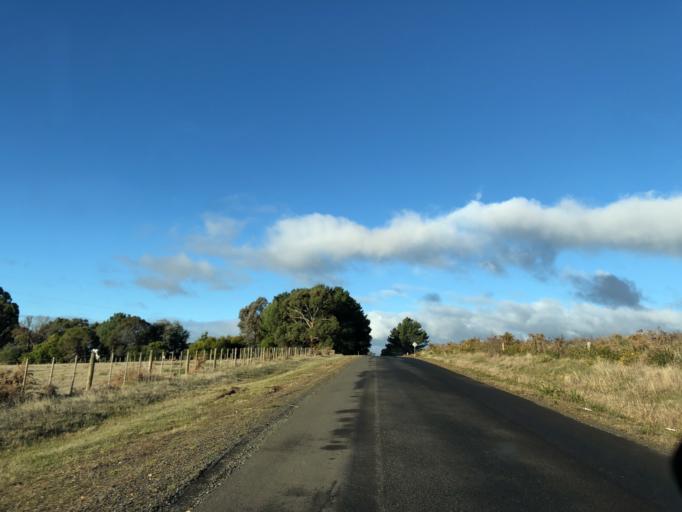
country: AU
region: Victoria
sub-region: Mount Alexander
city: Castlemaine
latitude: -37.2103
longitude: 144.3078
